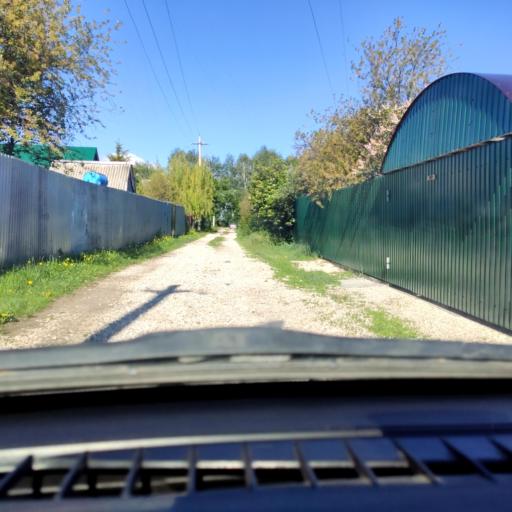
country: RU
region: Samara
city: Tol'yatti
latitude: 53.6279
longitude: 49.4044
